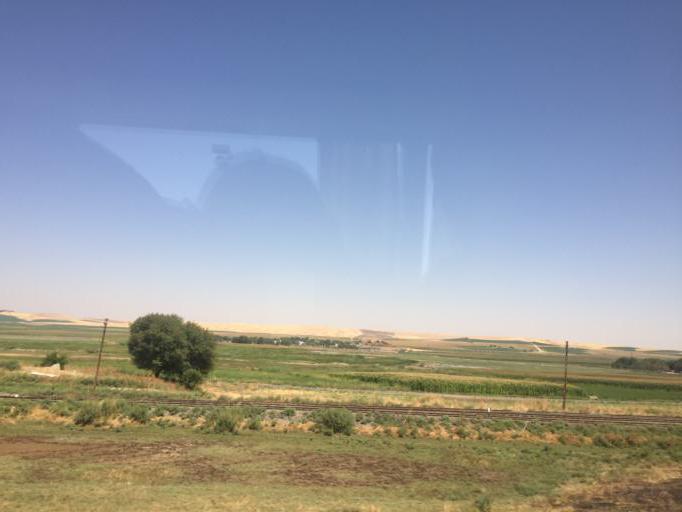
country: TR
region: Diyarbakir
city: Tepe
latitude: 37.8482
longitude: 40.8000
